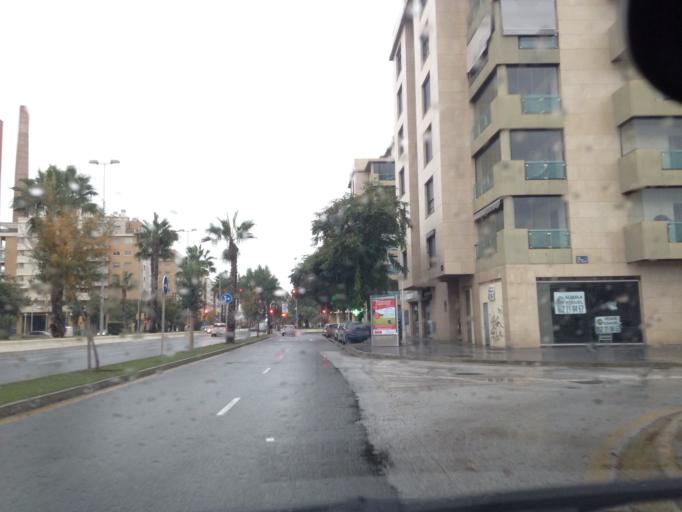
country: ES
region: Andalusia
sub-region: Provincia de Malaga
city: Malaga
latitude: 36.6952
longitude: -4.4399
